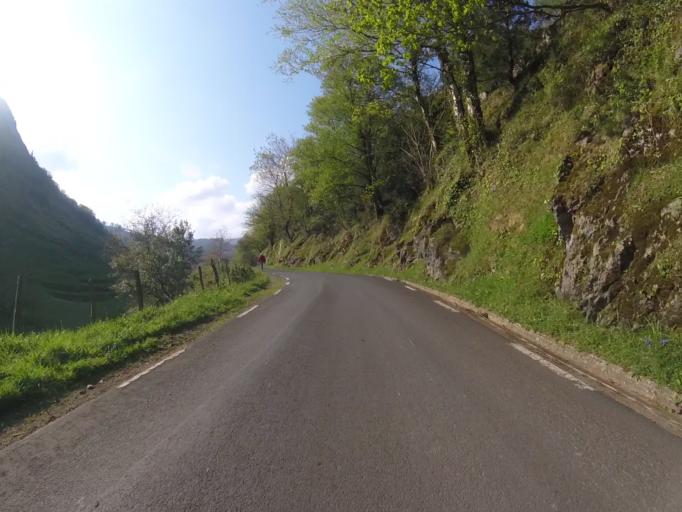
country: ES
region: Basque Country
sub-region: Provincia de Guipuzcoa
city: Azkoitia
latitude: 43.2358
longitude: -2.3242
